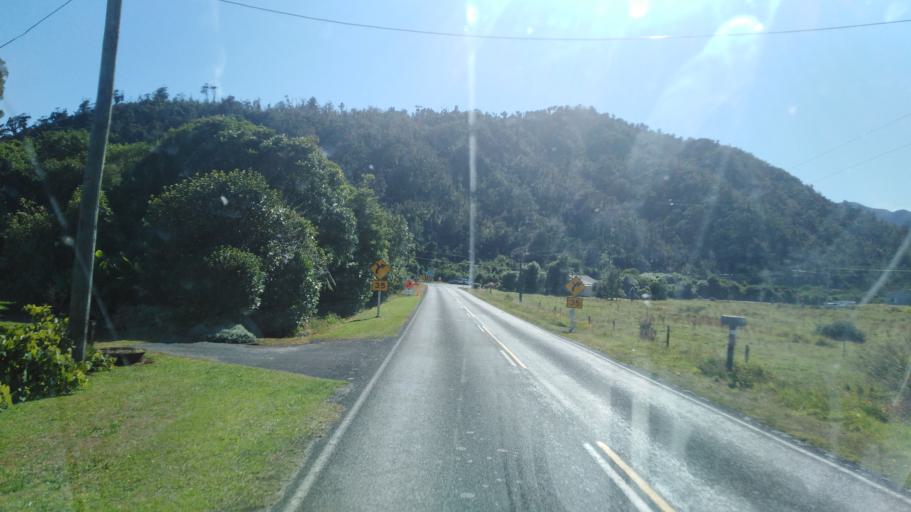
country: NZ
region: West Coast
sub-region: Buller District
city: Westport
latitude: -41.5300
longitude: 171.9427
